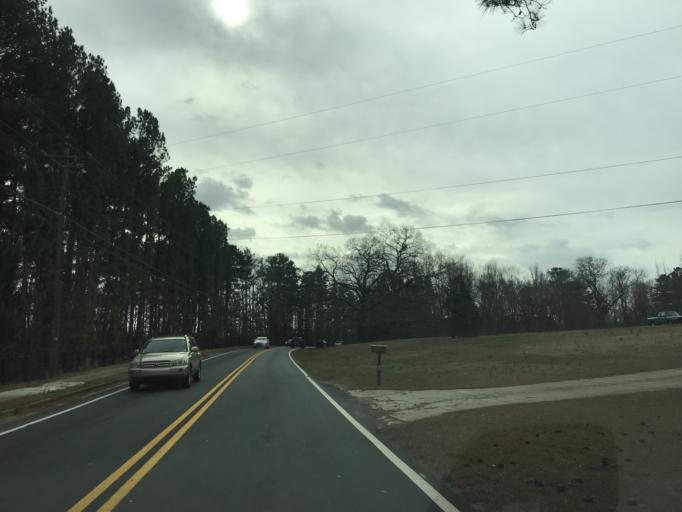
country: US
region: Georgia
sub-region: Fulton County
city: Milton
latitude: 34.1486
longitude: -84.2859
